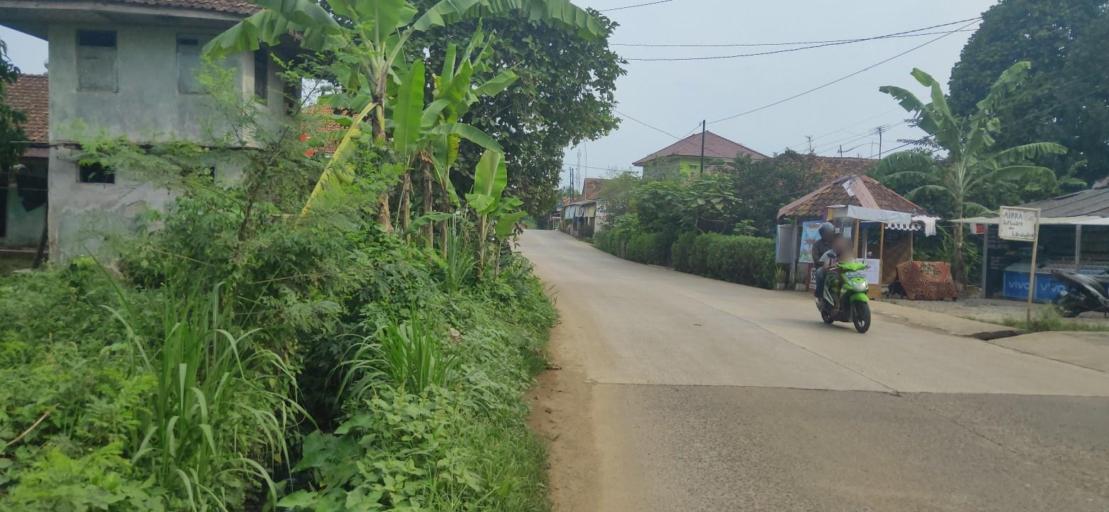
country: ID
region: West Java
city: Pangradin Satu
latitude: -6.4495
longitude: 106.4617
